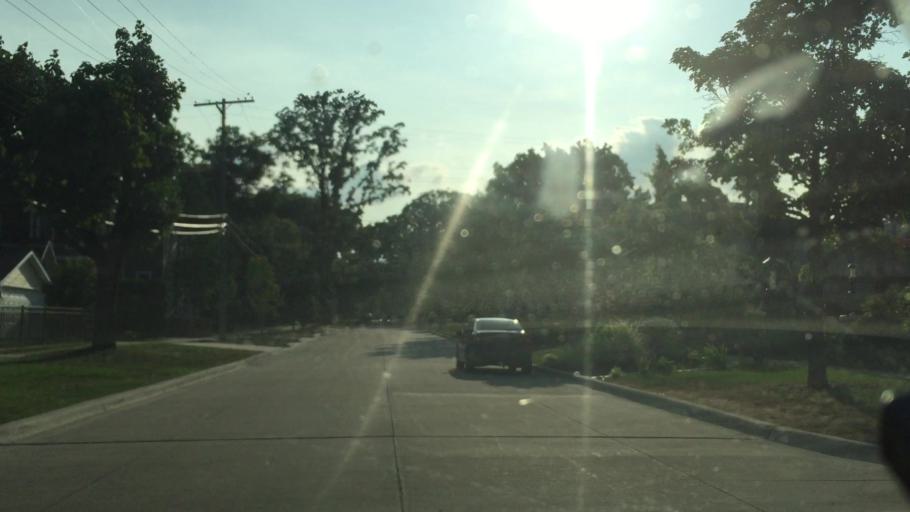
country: US
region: Michigan
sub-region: Oakland County
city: Beverly Hills
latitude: 42.5340
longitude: -83.2157
